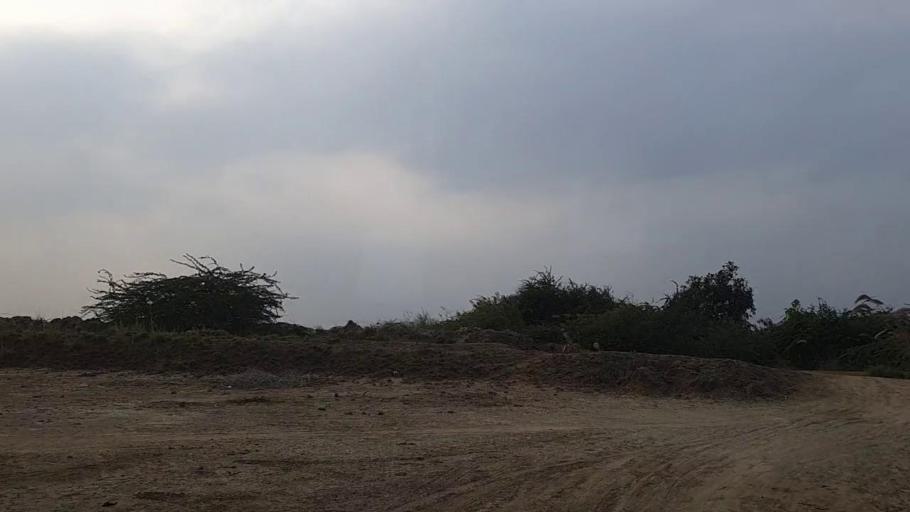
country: PK
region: Sindh
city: Mirpur Sakro
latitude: 24.6205
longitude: 67.5024
